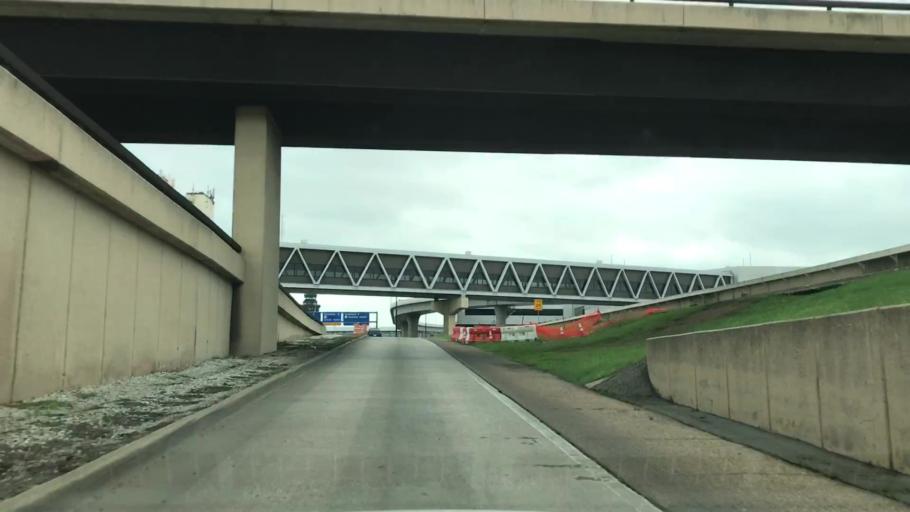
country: US
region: Texas
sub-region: Tarrant County
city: Grapevine
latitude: 32.9037
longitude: -97.0412
